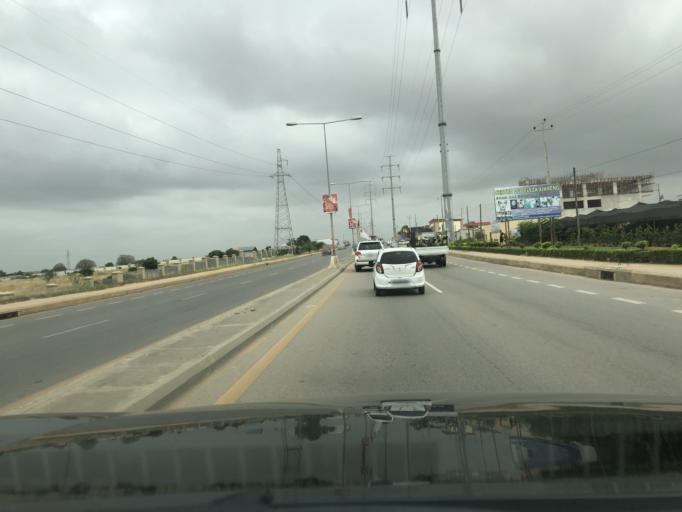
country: AO
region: Luanda
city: Luanda
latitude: -8.9668
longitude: 13.2063
